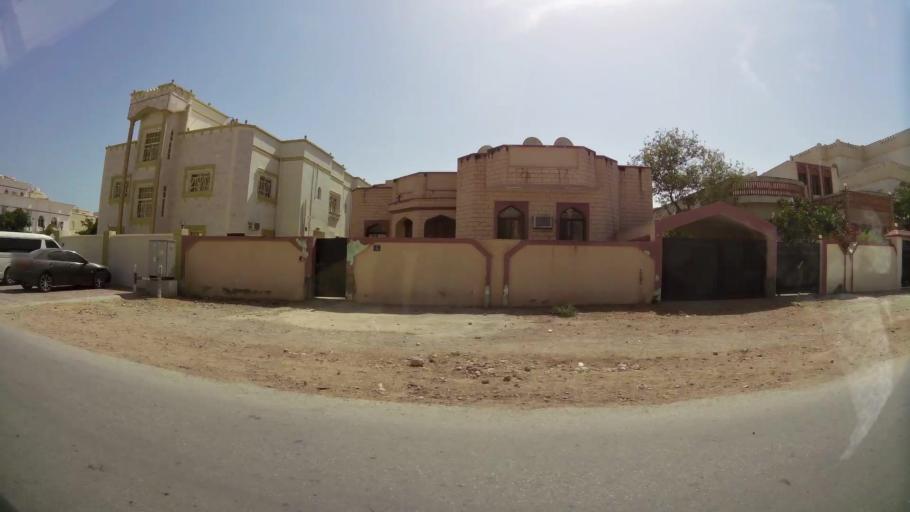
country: OM
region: Zufar
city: Salalah
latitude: 17.0462
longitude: 54.1513
